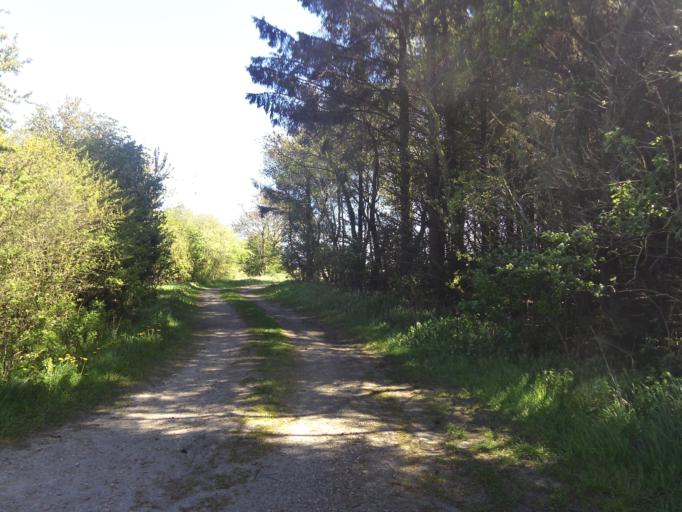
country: DK
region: South Denmark
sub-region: Tonder Kommune
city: Sherrebek
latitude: 55.2358
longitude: 8.7308
